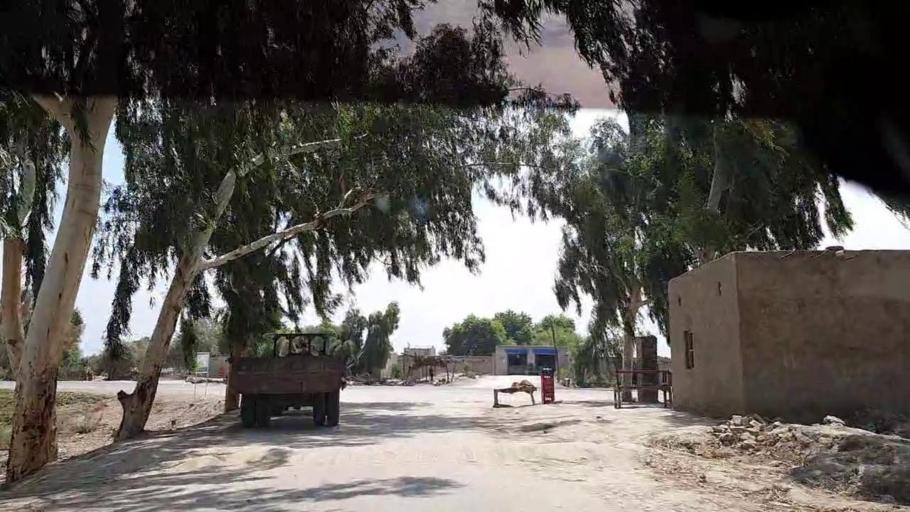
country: PK
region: Sindh
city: Ghauspur
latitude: 28.0884
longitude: 68.9636
